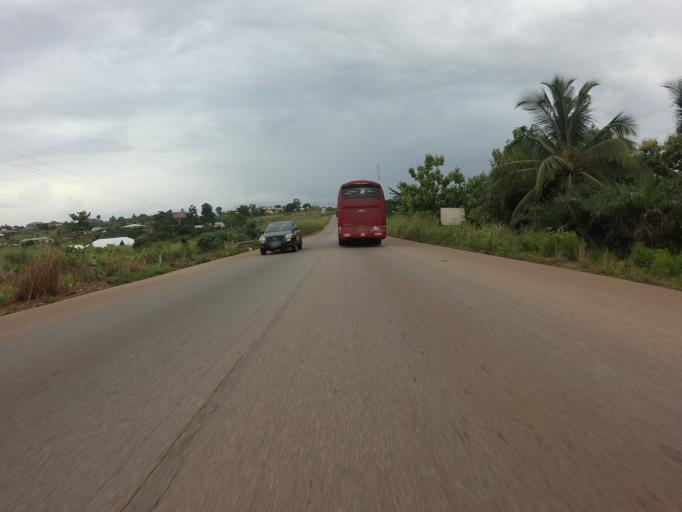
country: GH
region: Ashanti
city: Konongo
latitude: 6.6175
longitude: -1.1850
